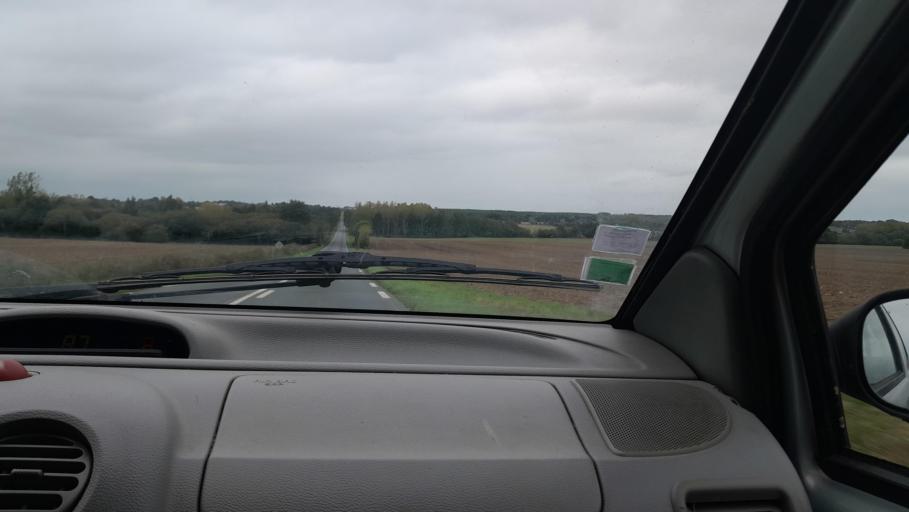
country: FR
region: Pays de la Loire
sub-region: Departement de la Loire-Atlantique
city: Saint-Mars-la-Jaille
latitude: 47.5549
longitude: -1.1860
